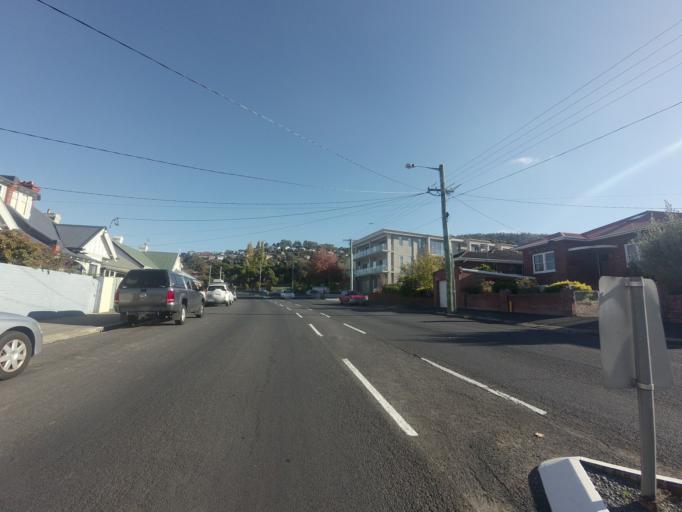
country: AU
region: Tasmania
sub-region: Hobart
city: Hobart
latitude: -42.8801
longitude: 147.3105
